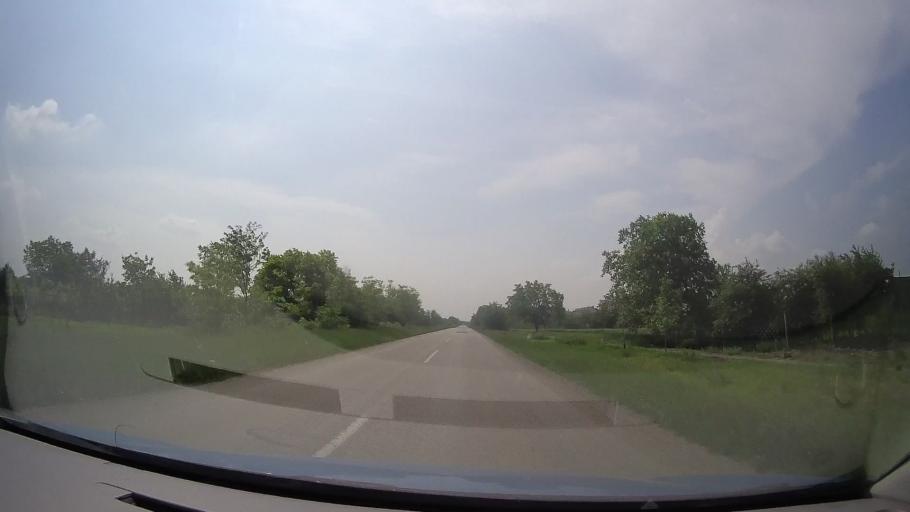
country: RS
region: Autonomna Pokrajina Vojvodina
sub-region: Juznobanatski Okrug
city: Kovacica
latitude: 45.0918
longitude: 20.6326
